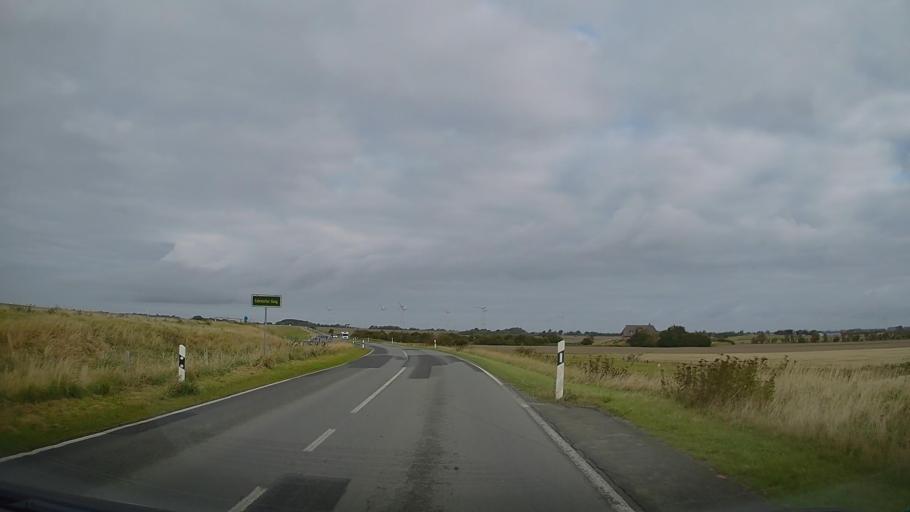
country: DE
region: Schleswig-Holstein
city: Galmsbull
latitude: 54.7039
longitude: 8.7554
